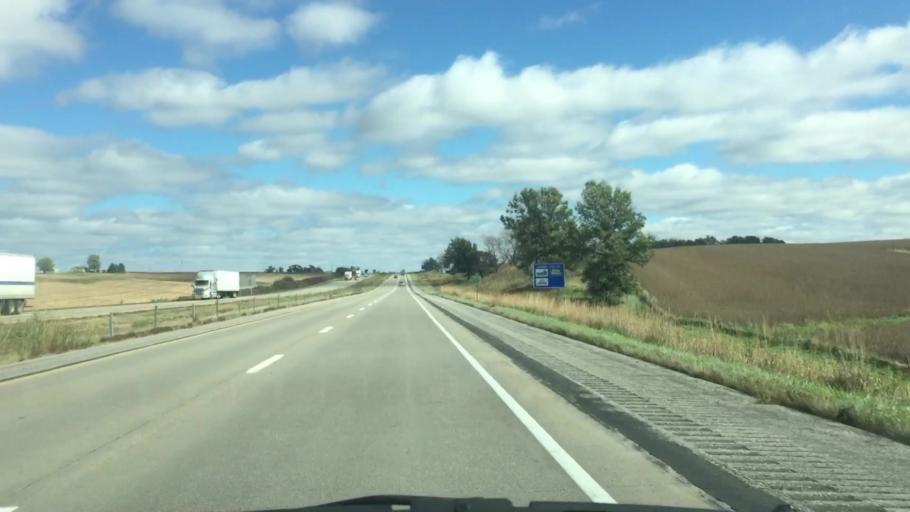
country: US
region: Iowa
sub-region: Iowa County
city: Williamsburg
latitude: 41.6871
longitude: -92.0459
